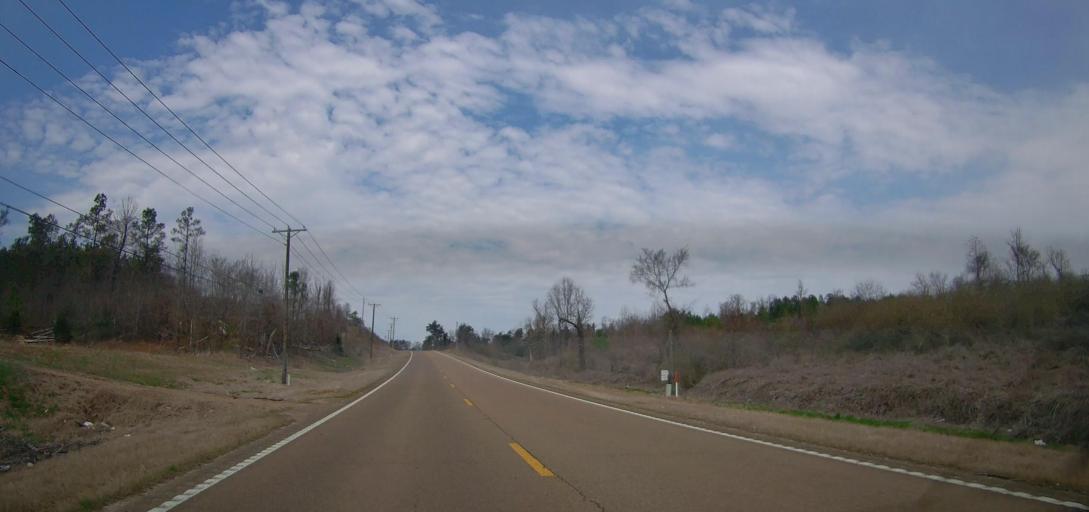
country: US
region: Mississippi
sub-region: Marshall County
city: Holly Springs
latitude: 34.7463
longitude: -89.4272
